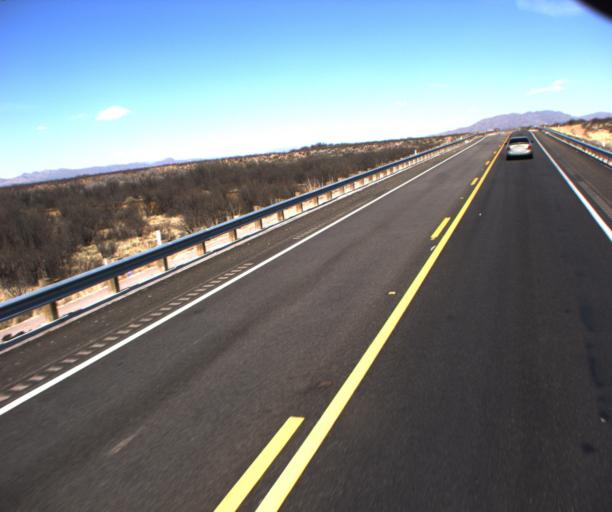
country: US
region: Arizona
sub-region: Cochise County
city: Sierra Vista Southeast
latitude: 31.5526
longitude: -110.1366
